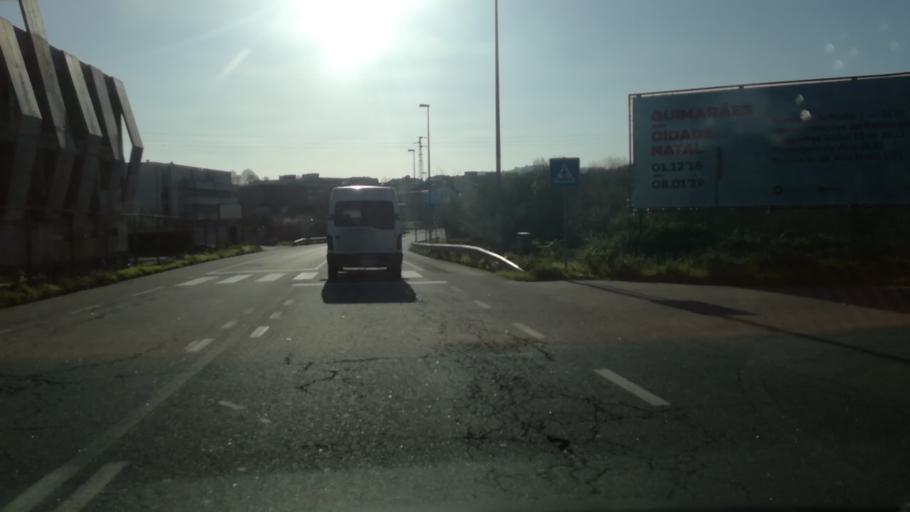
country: PT
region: Braga
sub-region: Guimaraes
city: Ponte
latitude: 41.4900
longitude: -8.3427
